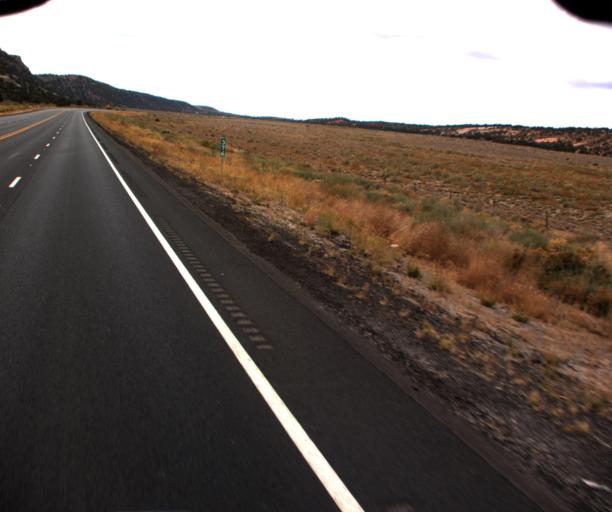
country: US
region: Arizona
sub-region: Navajo County
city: Kayenta
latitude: 36.5749
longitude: -110.4766
